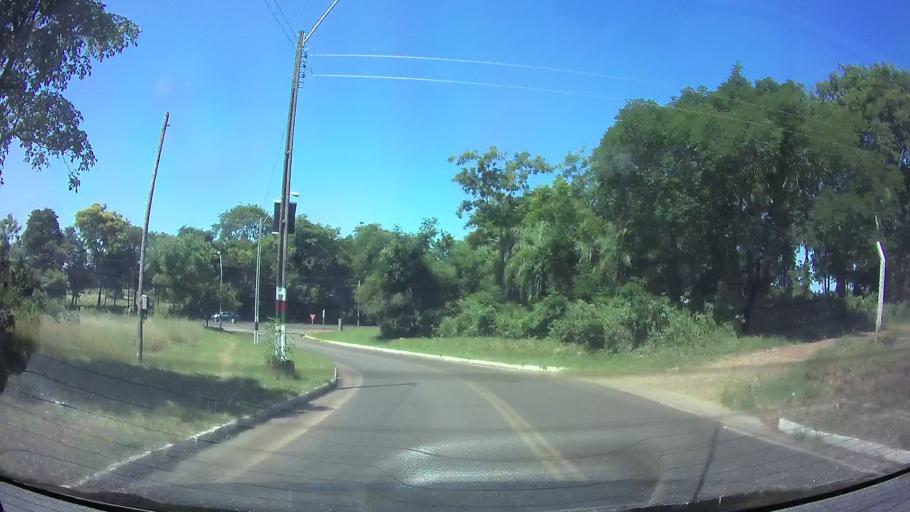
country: PY
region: Central
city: Aregua
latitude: -25.3054
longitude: -57.3956
